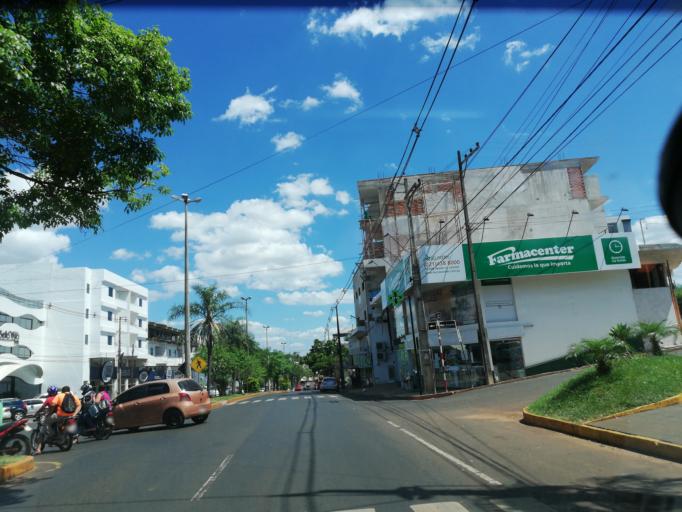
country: PY
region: Itapua
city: Encarnacion
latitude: -27.3415
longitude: -55.8579
